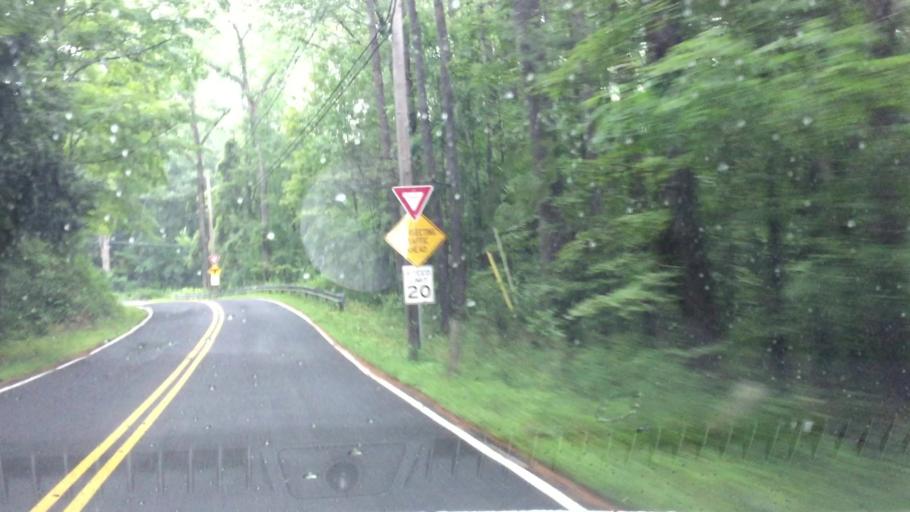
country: US
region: Massachusetts
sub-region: Berkshire County
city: Housatonic
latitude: 42.2949
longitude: -73.3860
